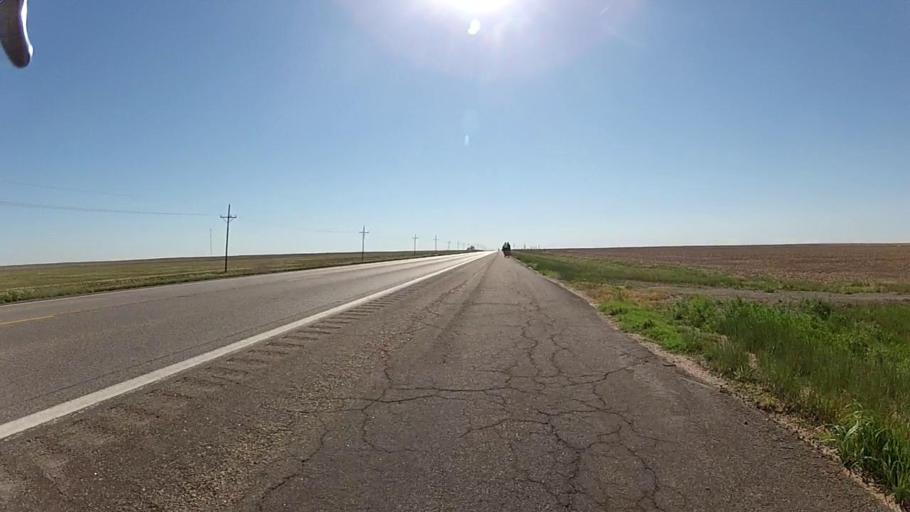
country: US
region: Kansas
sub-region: Kiowa County
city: Greensburg
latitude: 37.5863
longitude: -99.6239
